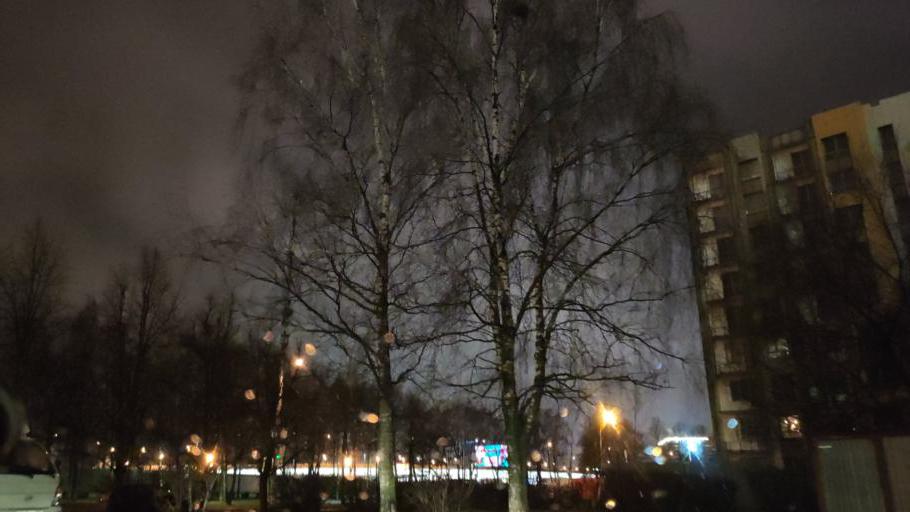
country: RU
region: Moskovskaya
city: Marfino
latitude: 55.7158
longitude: 37.3912
